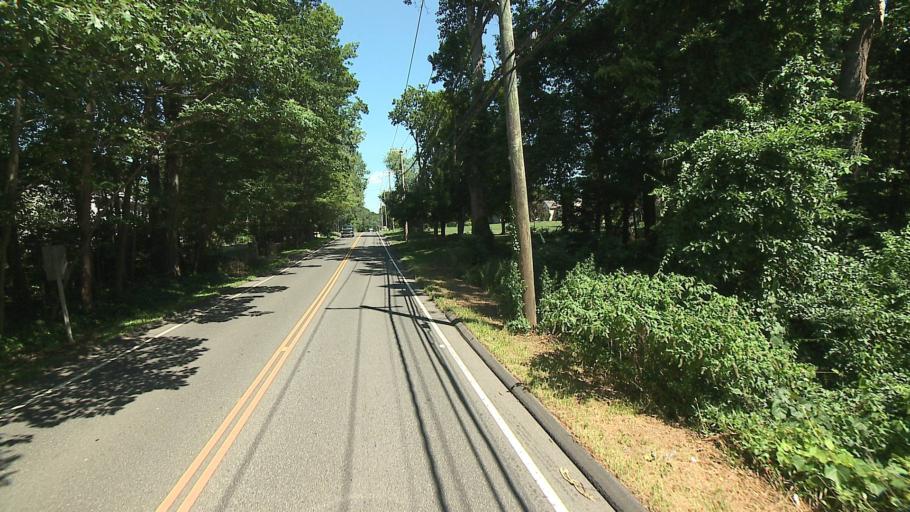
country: US
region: Connecticut
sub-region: Fairfield County
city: Trumbull
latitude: 41.3522
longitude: -73.1974
